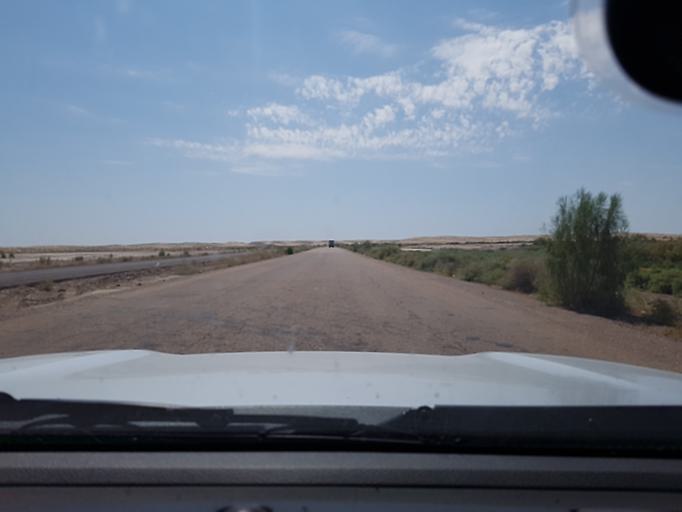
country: TM
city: Akdepe
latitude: 41.5453
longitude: 58.5760
